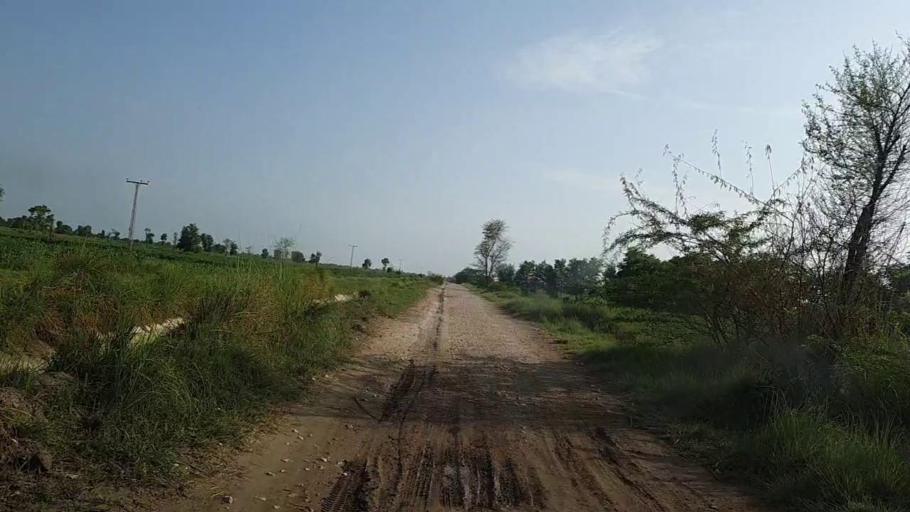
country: PK
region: Sindh
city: Pad Idan
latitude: 26.8323
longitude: 68.2423
